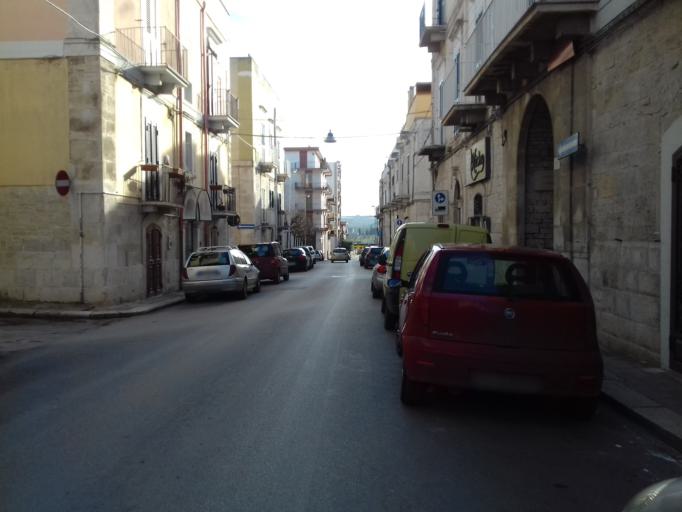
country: IT
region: Apulia
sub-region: Provincia di Bari
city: Ruvo di Puglia
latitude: 41.1155
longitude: 16.4823
